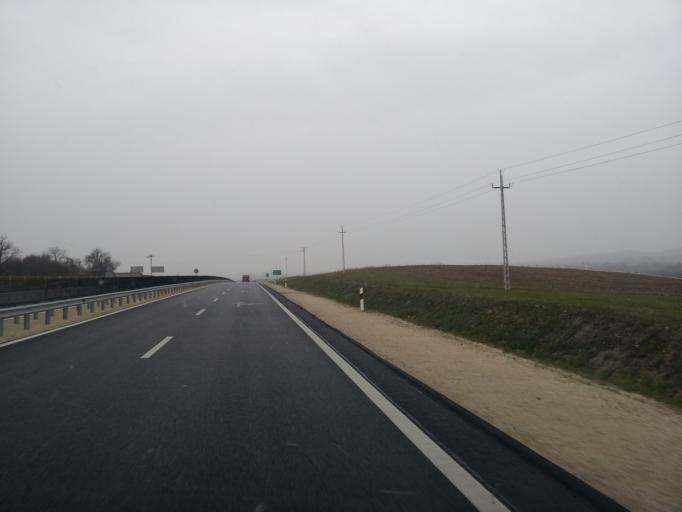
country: HU
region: Veszprem
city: Herend
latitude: 47.1265
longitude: 17.7737
